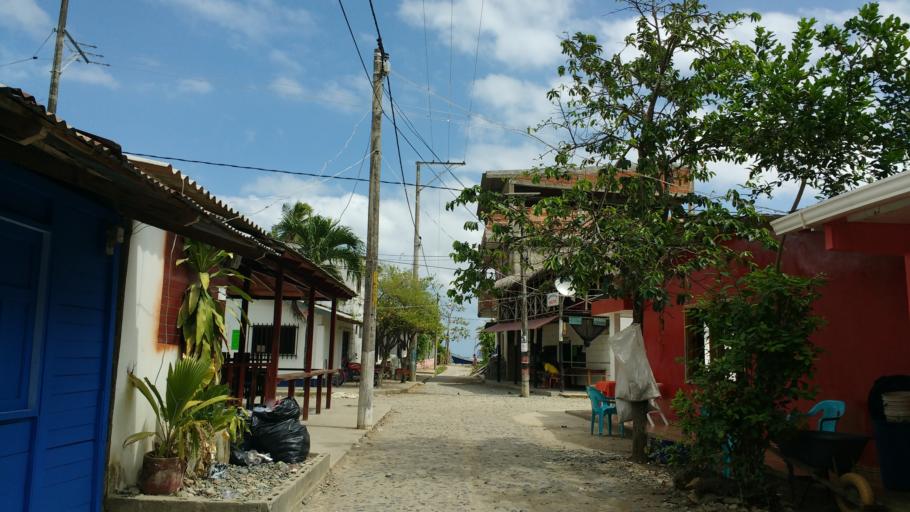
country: PA
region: Guna Yala
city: Puerto Obaldia
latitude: 8.6373
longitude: -77.3471
